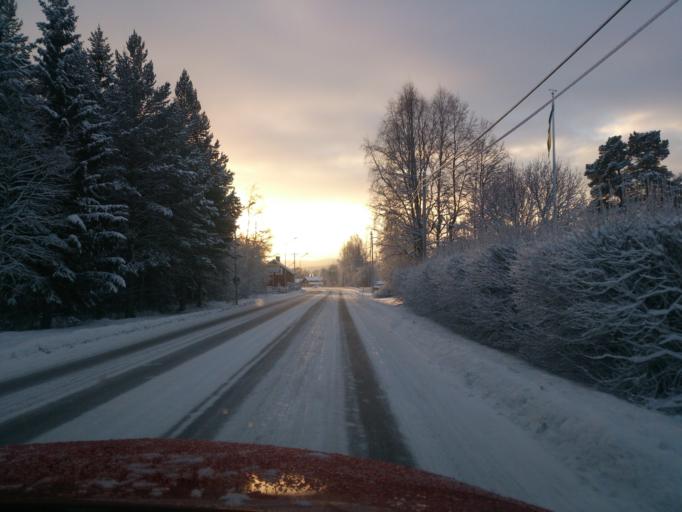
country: SE
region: Jaemtland
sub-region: Harjedalens Kommun
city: Sveg
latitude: 62.4559
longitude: 13.8633
